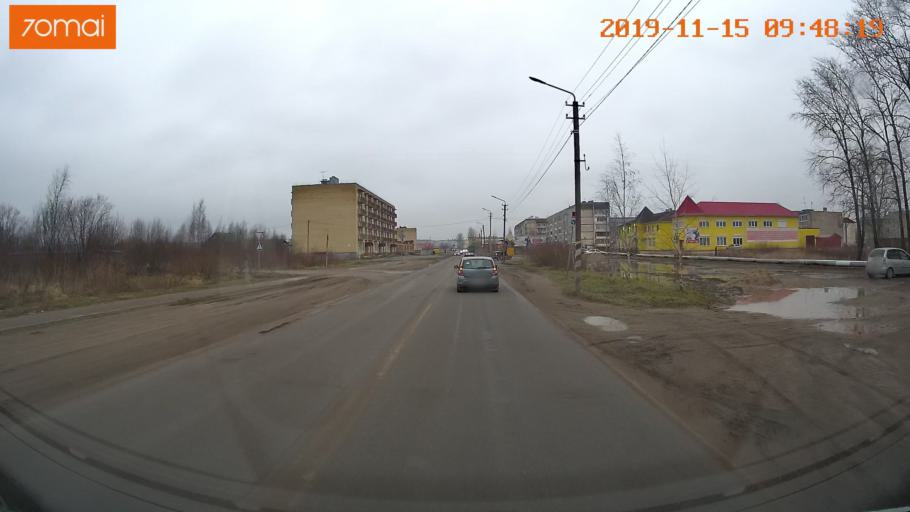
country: RU
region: Vologda
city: Sheksna
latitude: 59.2224
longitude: 38.5125
